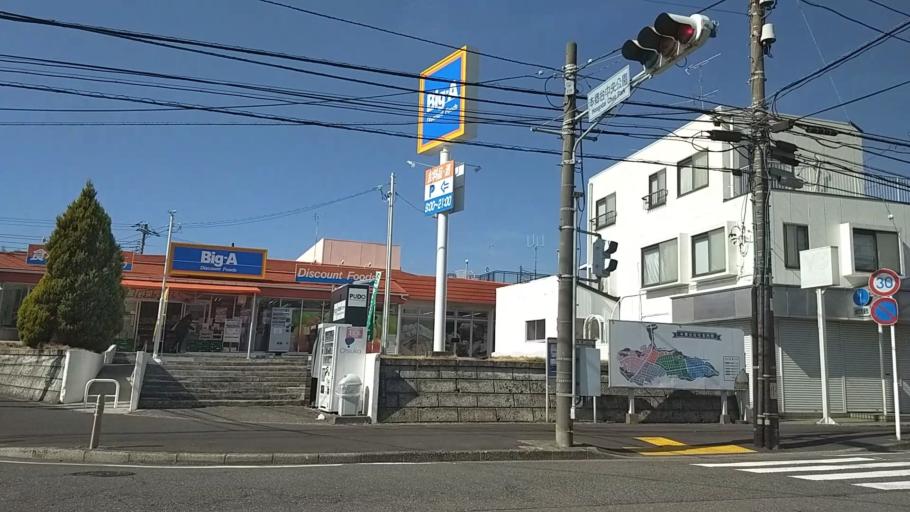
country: JP
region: Kanagawa
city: Kamakura
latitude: 35.3721
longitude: 139.5461
